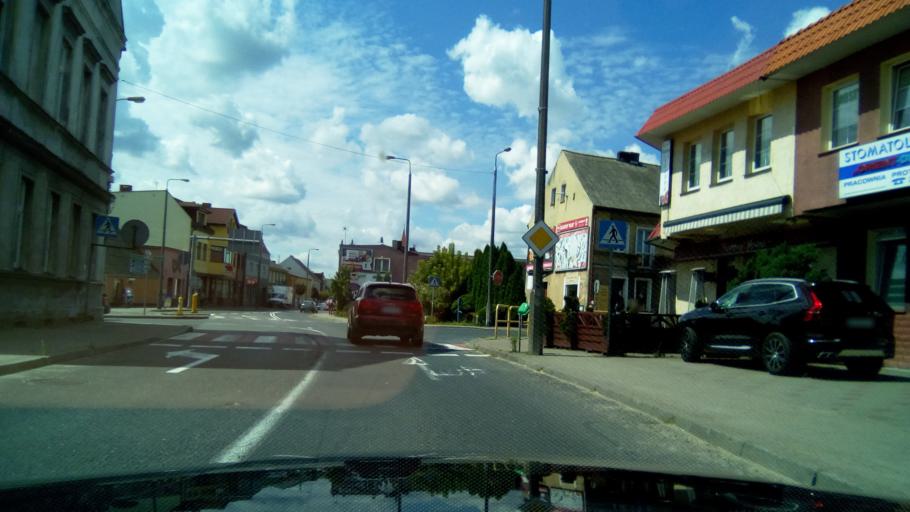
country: PL
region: Kujawsko-Pomorskie
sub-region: Powiat nakielski
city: Szubin
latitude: 53.0096
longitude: 17.7404
